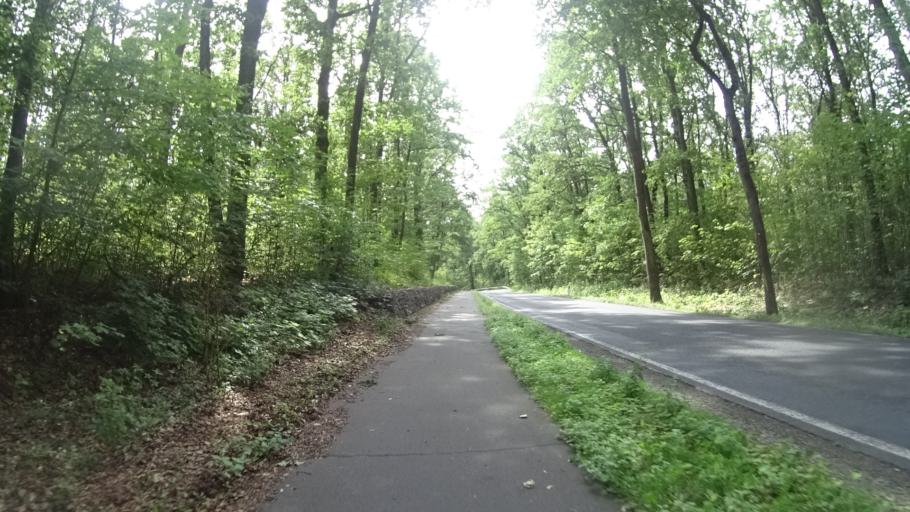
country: DE
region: Brandenburg
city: Borkwalde
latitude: 52.3061
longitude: 12.7642
